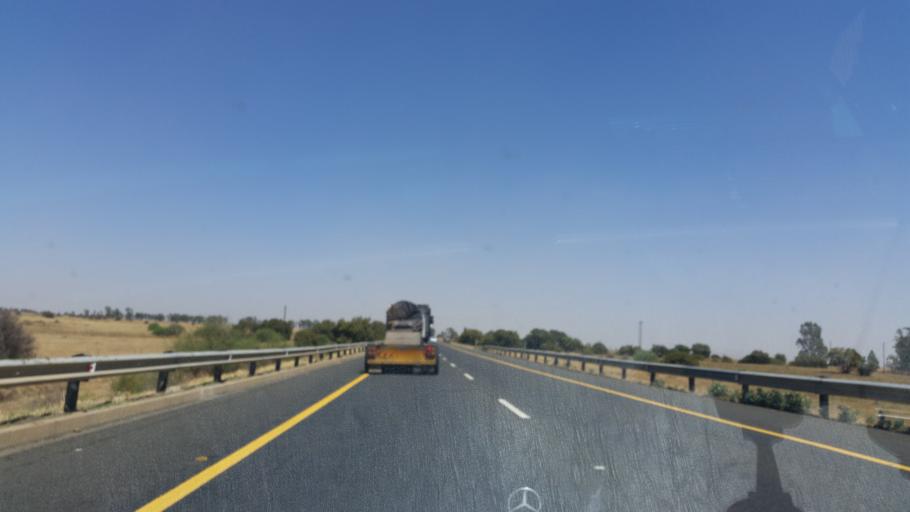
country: ZA
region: Orange Free State
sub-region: Lejweleputswa District Municipality
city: Winburg
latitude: -28.6343
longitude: 26.8997
